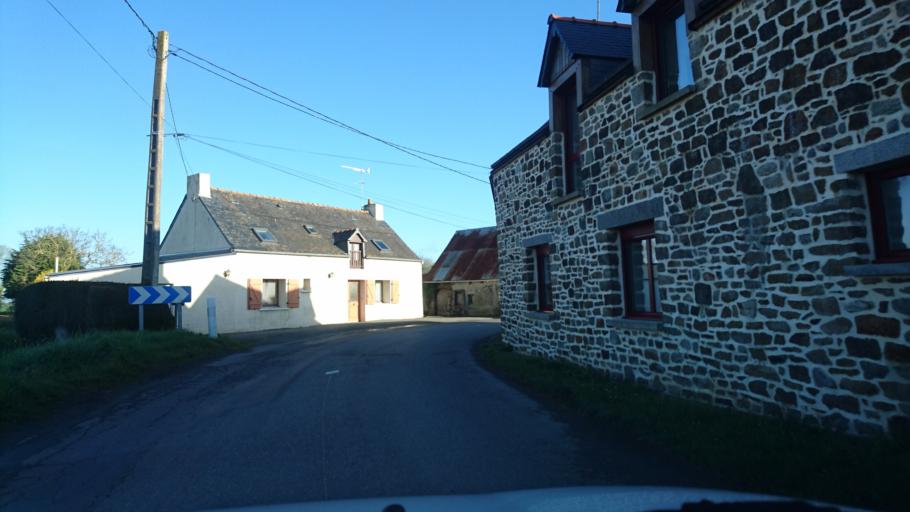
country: FR
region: Brittany
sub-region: Departement d'Ille-et-Vilaine
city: Cherrueix
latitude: 48.5901
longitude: -1.7198
